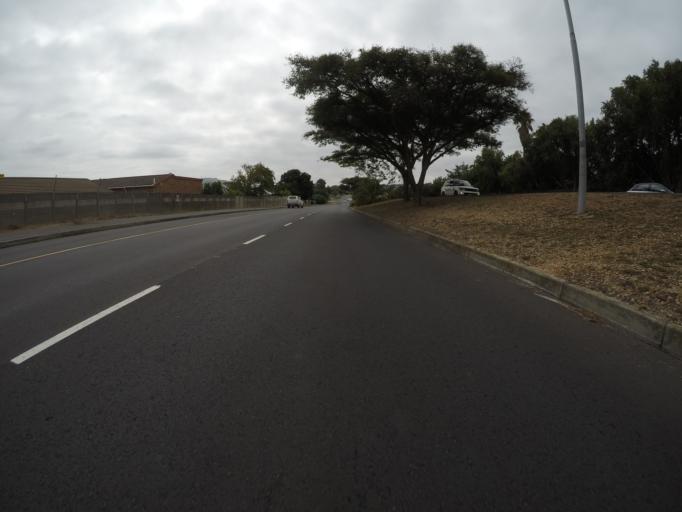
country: ZA
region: Western Cape
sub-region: City of Cape Town
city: Kraaifontein
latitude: -33.8652
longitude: 18.6329
